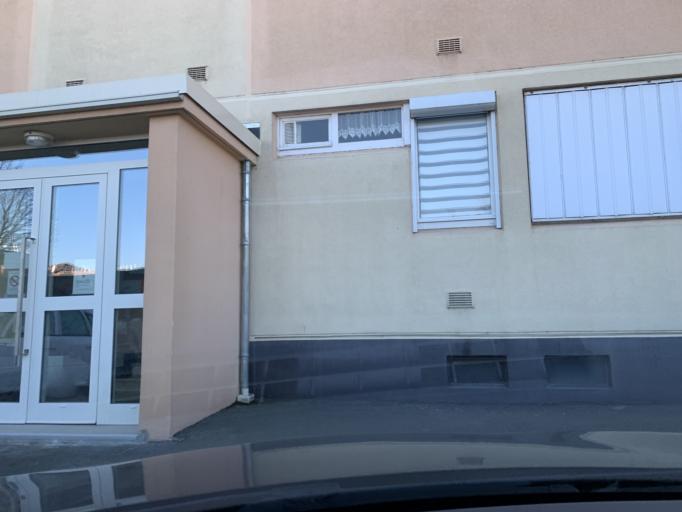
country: FR
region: Nord-Pas-de-Calais
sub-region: Departement du Nord
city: Neuville-Saint-Remy
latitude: 50.1795
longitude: 3.2279
